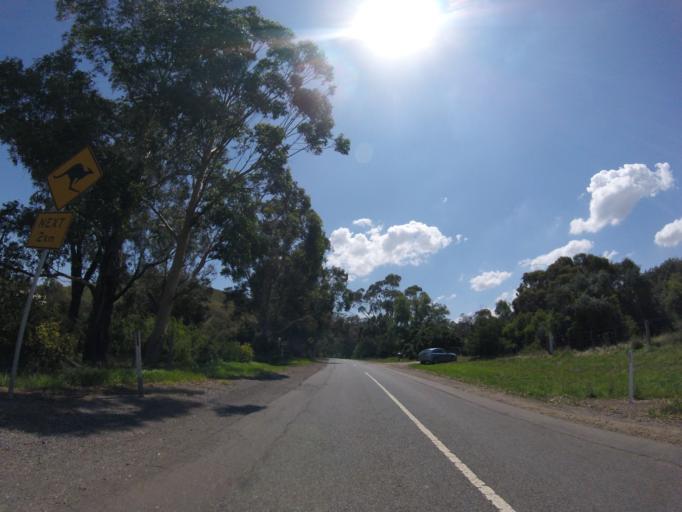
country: AU
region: Victoria
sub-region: Hume
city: Greenvale
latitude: -37.6114
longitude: 144.8027
